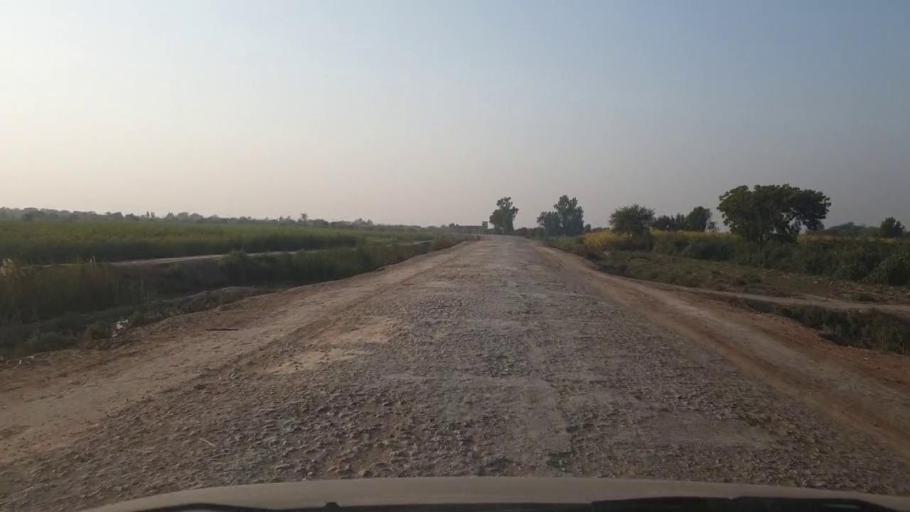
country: PK
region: Sindh
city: Mirwah Gorchani
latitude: 25.3700
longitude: 69.1308
